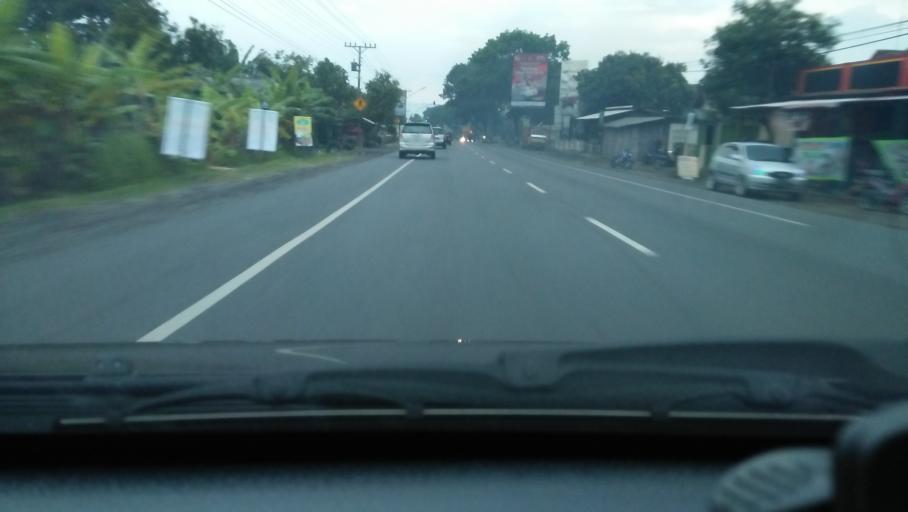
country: ID
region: Central Java
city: Magelang
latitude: -7.4045
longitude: 110.2397
